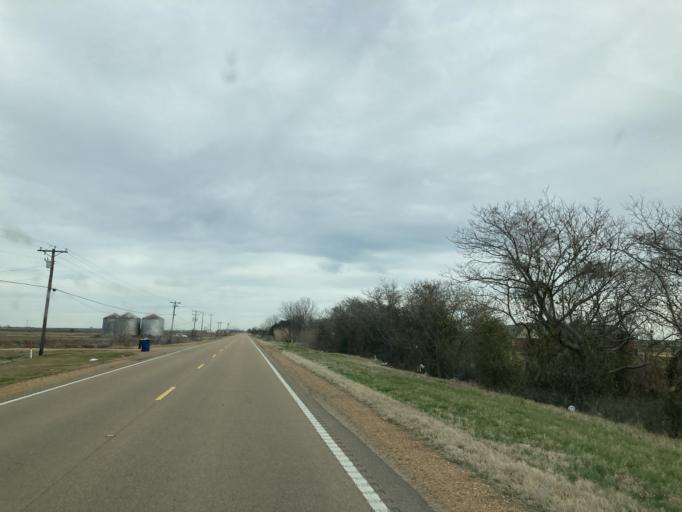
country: US
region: Mississippi
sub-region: Humphreys County
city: Belzoni
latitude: 33.1837
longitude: -90.5782
